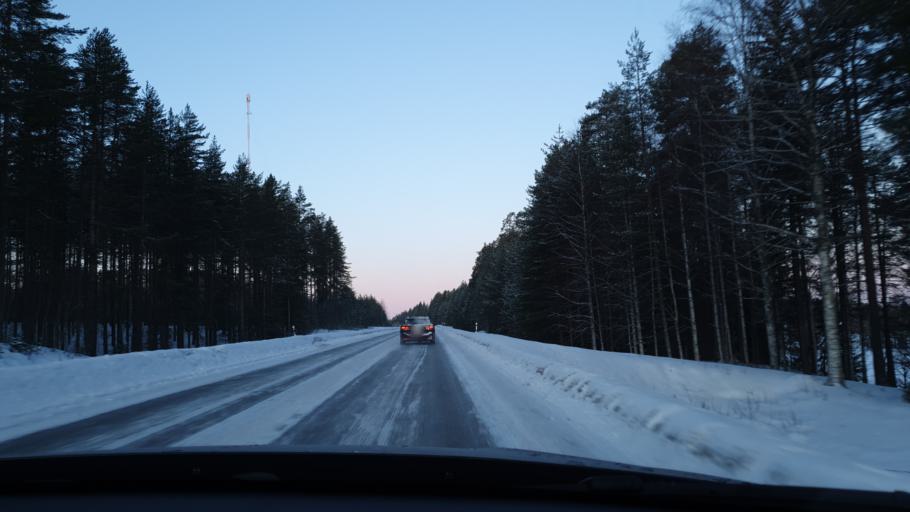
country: FI
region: Kainuu
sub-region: Kajaani
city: Sotkamo
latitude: 64.1114
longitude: 28.4789
